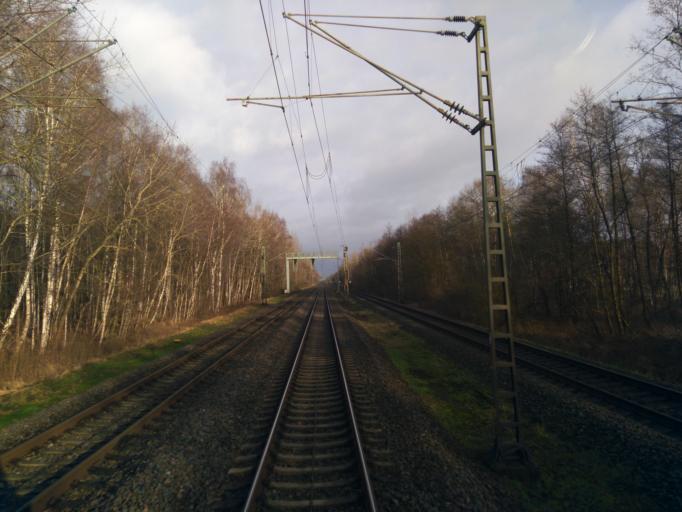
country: DE
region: Lower Saxony
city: Konigsmoor
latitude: 53.2375
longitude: 9.6573
